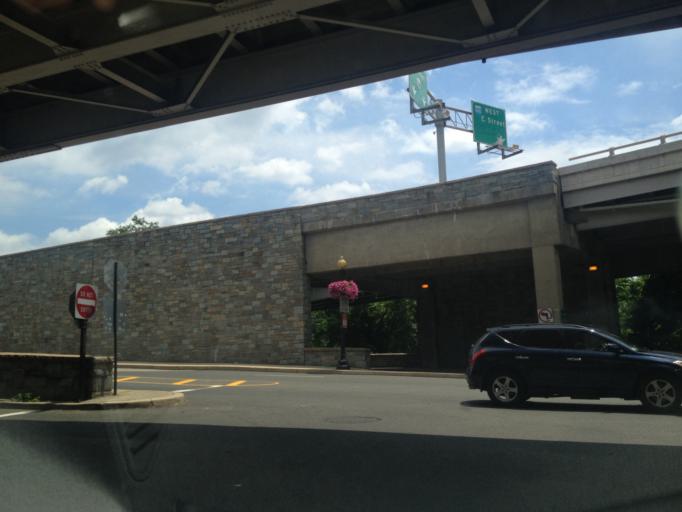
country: US
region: Washington, D.C.
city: Washington, D.C.
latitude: 38.9027
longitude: -77.0580
